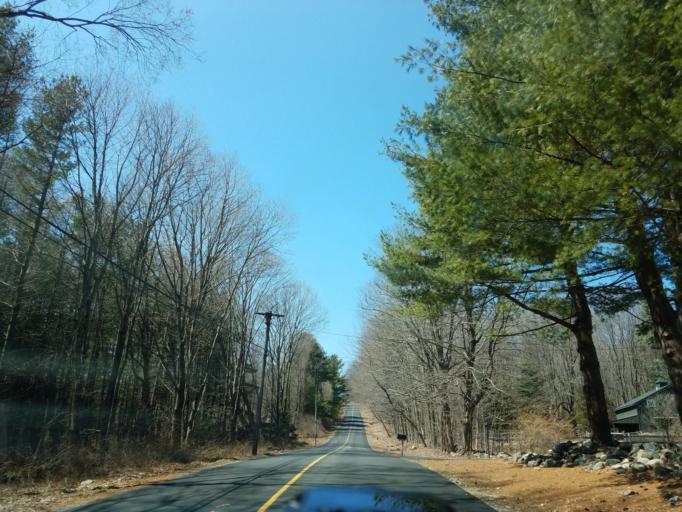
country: US
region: Connecticut
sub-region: Litchfield County
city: Bethlehem Village
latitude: 41.6289
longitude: -73.2381
